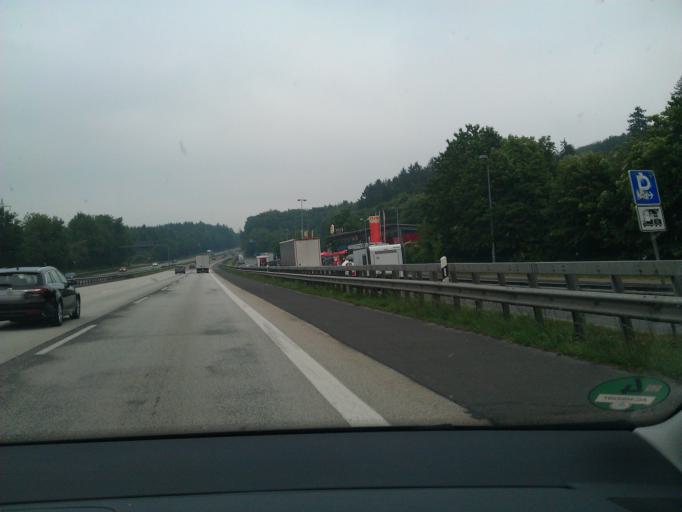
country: DE
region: Rheinland-Pfalz
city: Heiligenroth
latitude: 50.4548
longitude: 7.8696
